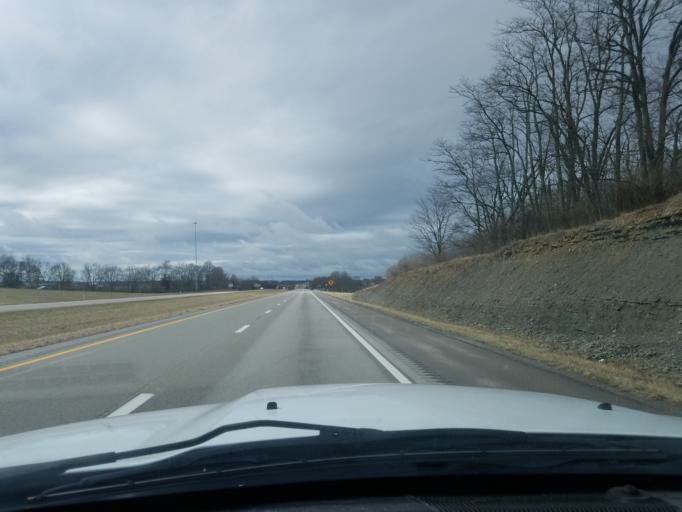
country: US
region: Kentucky
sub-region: Montgomery County
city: Mount Sterling
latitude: 38.0886
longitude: -83.8993
